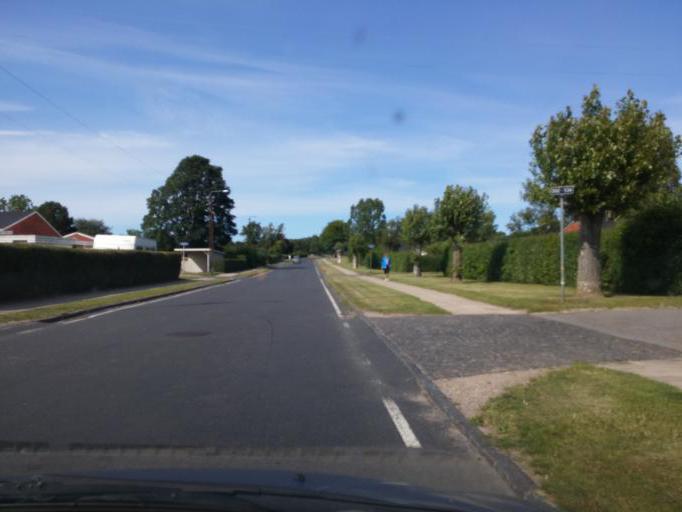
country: DK
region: South Denmark
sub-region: Kerteminde Kommune
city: Munkebo
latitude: 55.4627
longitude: 10.5626
